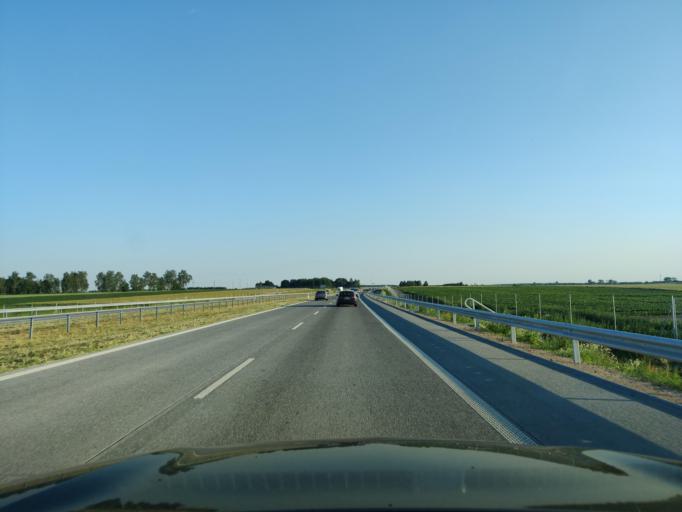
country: PL
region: Masovian Voivodeship
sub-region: Powiat mlawski
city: Wisniewo
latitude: 53.0423
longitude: 20.3575
